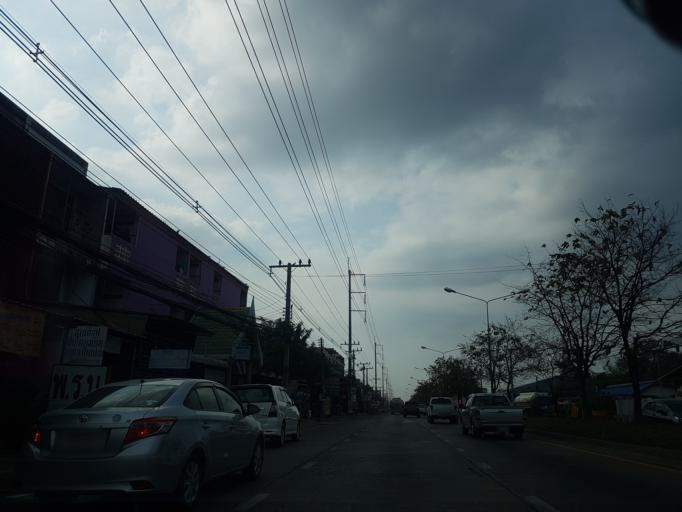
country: TH
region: Sara Buri
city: Phra Phutthabat
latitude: 14.7303
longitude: 100.7867
